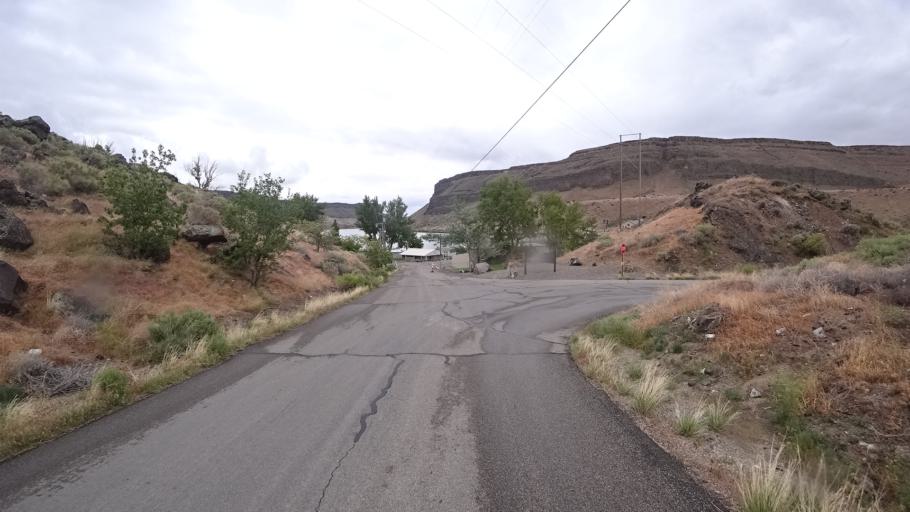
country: US
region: Idaho
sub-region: Owyhee County
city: Murphy
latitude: 43.2448
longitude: -116.3770
